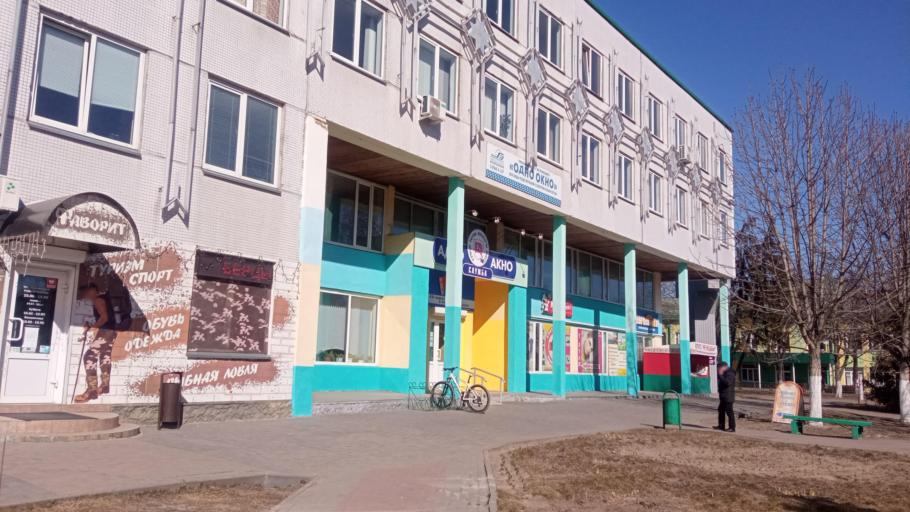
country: BY
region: Gomel
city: Horad Rechytsa
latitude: 52.3674
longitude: 30.3951
